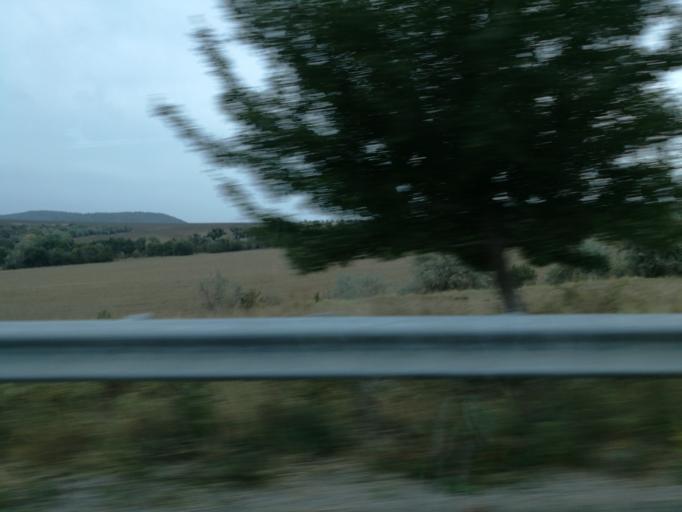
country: RO
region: Tulcea
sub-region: Comuna Horia
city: Horia
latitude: 44.9834
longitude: 28.4506
